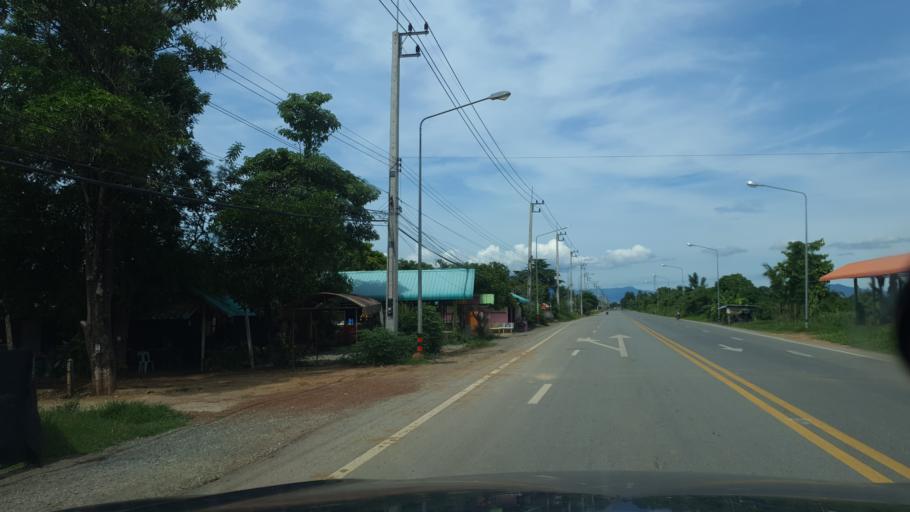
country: TH
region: Sukhothai
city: Sukhothai
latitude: 17.0601
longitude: 99.8283
